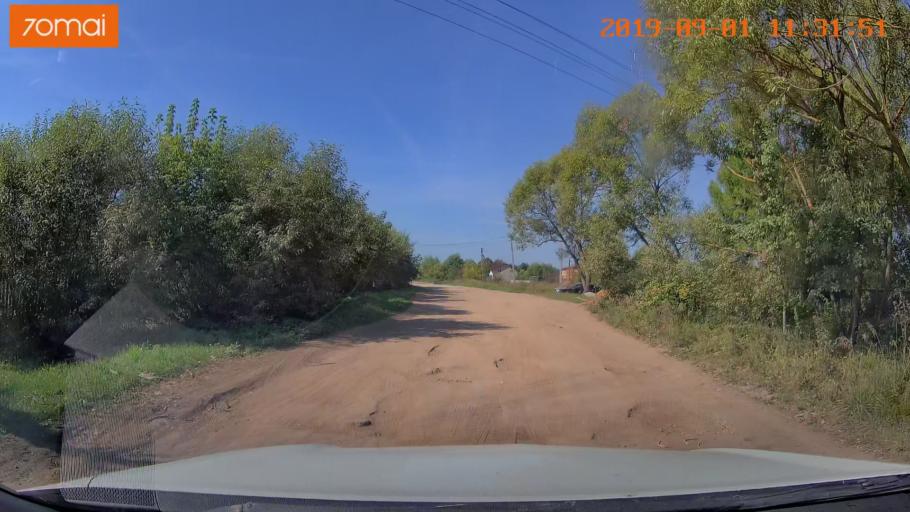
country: RU
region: Kaluga
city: Detchino
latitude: 54.8352
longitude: 36.3363
